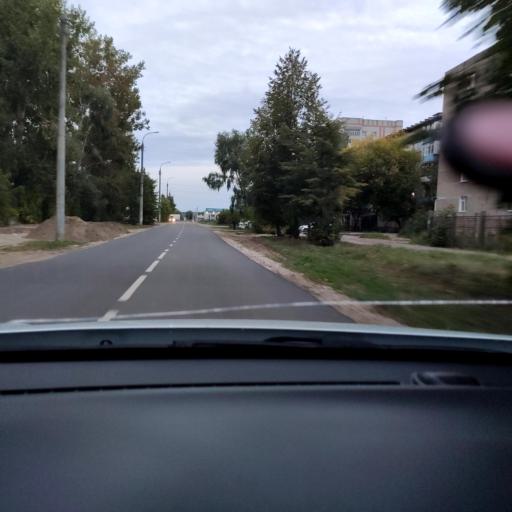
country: RU
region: Mariy-El
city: Volzhsk
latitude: 55.8676
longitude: 48.3444
